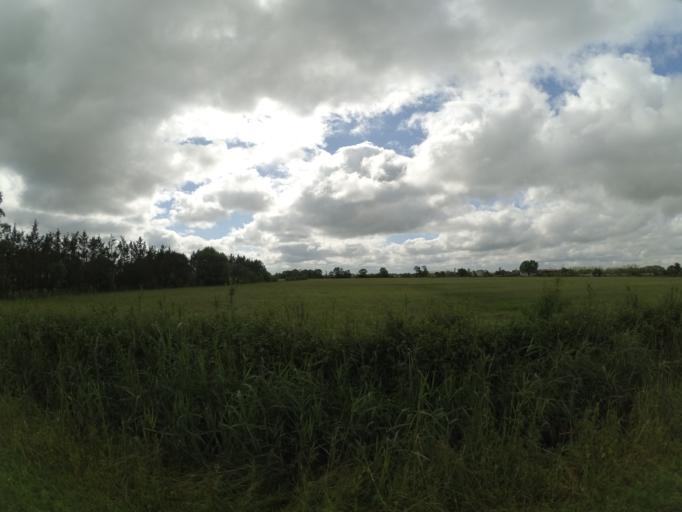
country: FR
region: Aquitaine
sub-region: Departement de la Gironde
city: Ludon-Medoc
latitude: 44.9914
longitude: -0.5852
